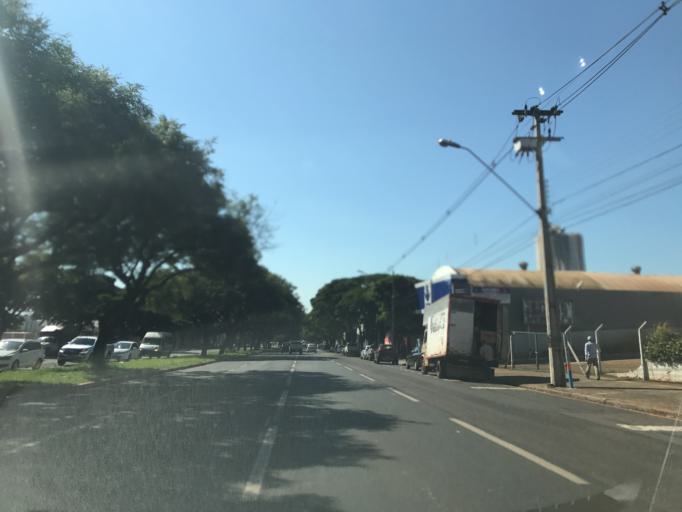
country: BR
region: Parana
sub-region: Maringa
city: Maringa
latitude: -23.4159
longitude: -51.9543
